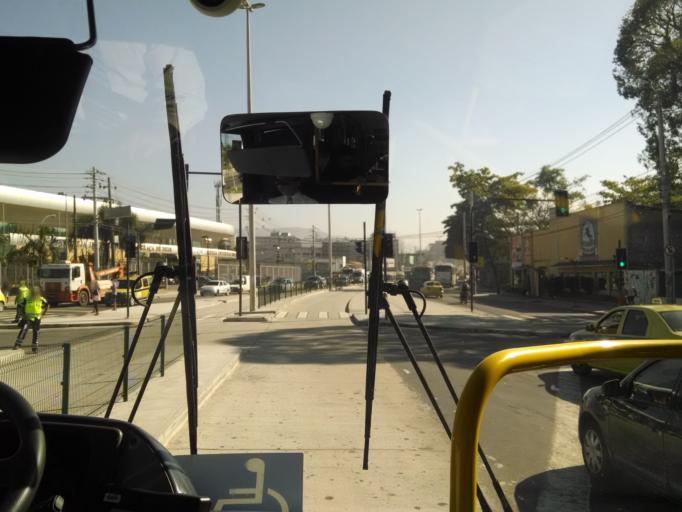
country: BR
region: Rio de Janeiro
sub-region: Sao Joao De Meriti
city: Sao Joao de Meriti
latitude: -22.9330
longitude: -43.3729
